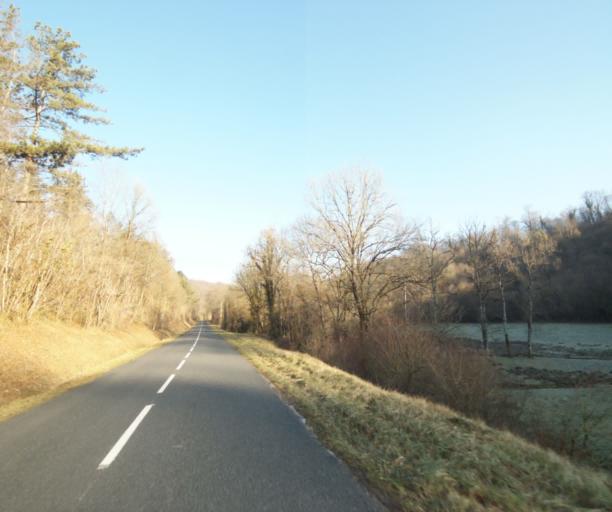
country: FR
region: Champagne-Ardenne
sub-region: Departement de la Haute-Marne
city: Chevillon
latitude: 48.5270
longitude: 5.1705
